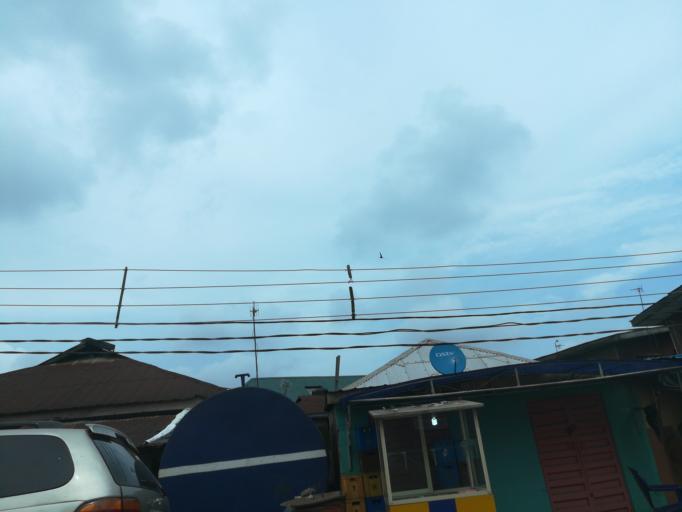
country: NG
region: Lagos
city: Oshodi
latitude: 6.5620
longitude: 3.3472
